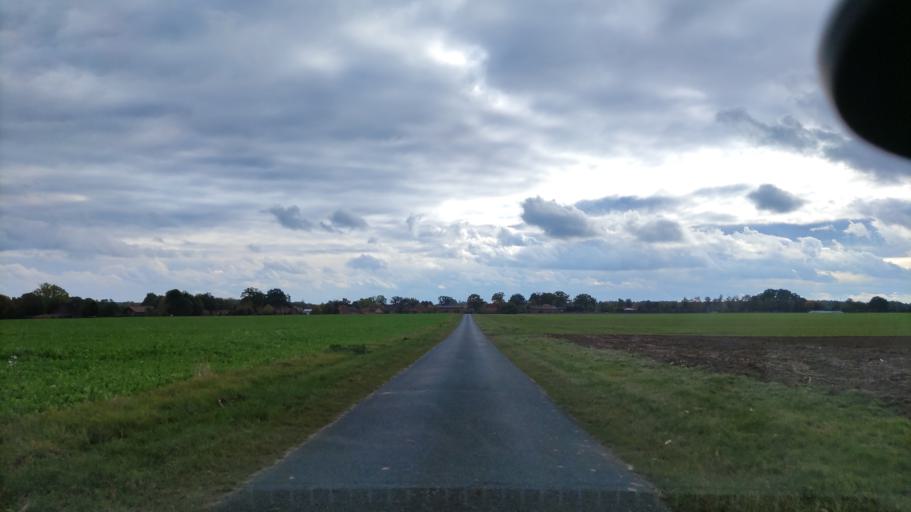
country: DE
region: Lower Saxony
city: Vastorf
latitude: 53.1514
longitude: 10.5348
